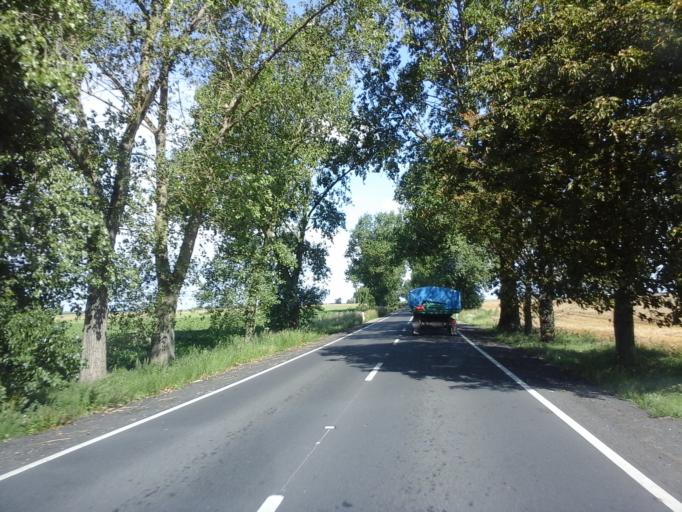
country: PL
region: West Pomeranian Voivodeship
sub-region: Powiat stargardzki
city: Stargard Szczecinski
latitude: 53.2541
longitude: 15.1010
